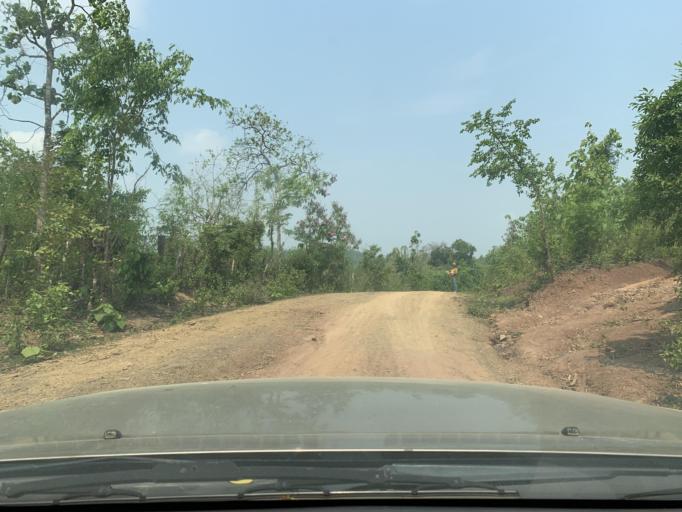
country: LA
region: Louangphabang
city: Louangphabang
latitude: 19.9378
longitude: 102.1466
